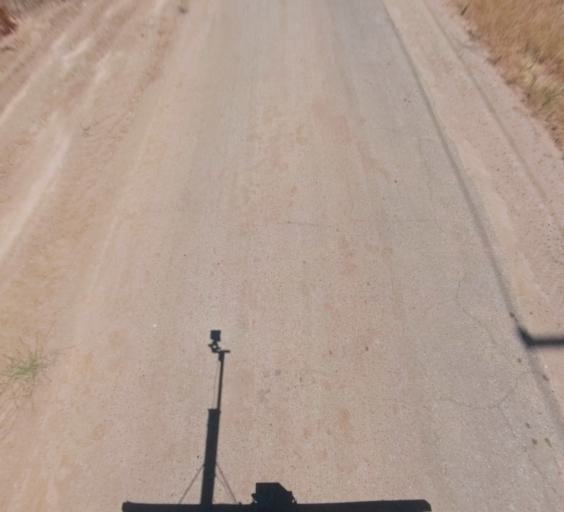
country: US
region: California
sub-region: Madera County
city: Bonadelle Ranchos-Madera Ranchos
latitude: 36.9411
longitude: -119.8306
